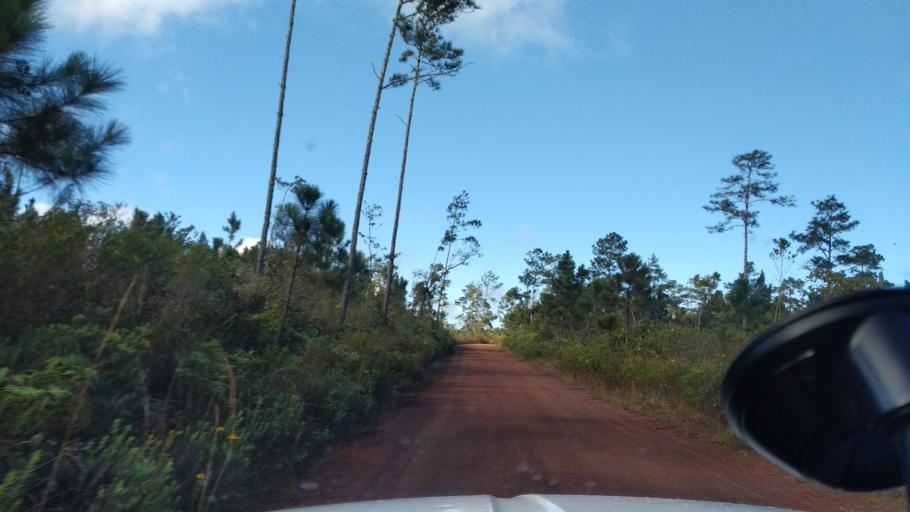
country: BZ
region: Cayo
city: Belmopan
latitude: 16.9980
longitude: -88.8420
